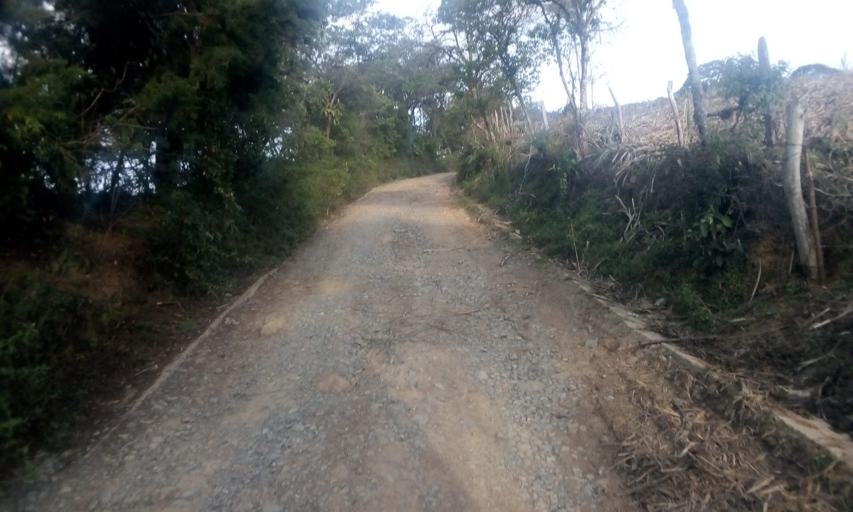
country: CO
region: Boyaca
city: Santana
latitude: 6.0148
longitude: -73.5114
